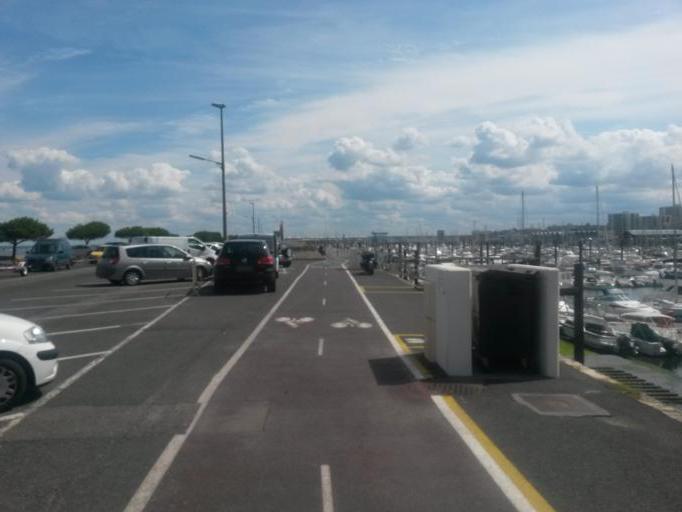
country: FR
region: Aquitaine
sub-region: Departement de la Gironde
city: Arcachon
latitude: 44.6621
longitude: -1.1500
